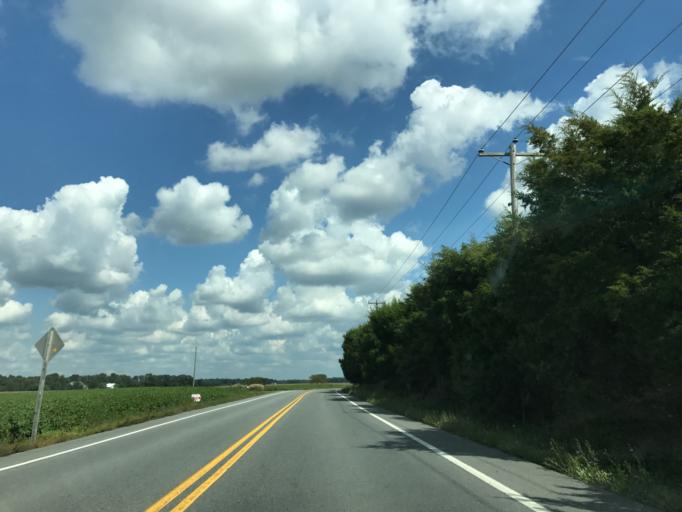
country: US
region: Maryland
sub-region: Caroline County
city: Ridgely
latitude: 39.0221
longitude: -75.9207
